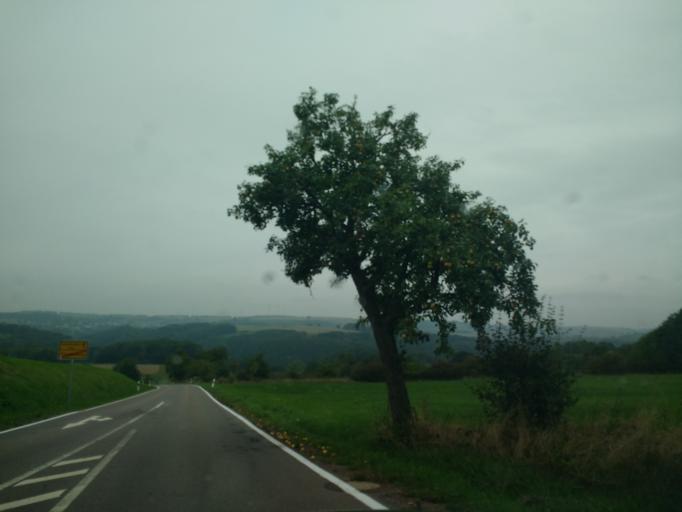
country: DE
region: Rheinland-Pfalz
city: Freudenburg
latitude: 49.5441
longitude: 6.5259
